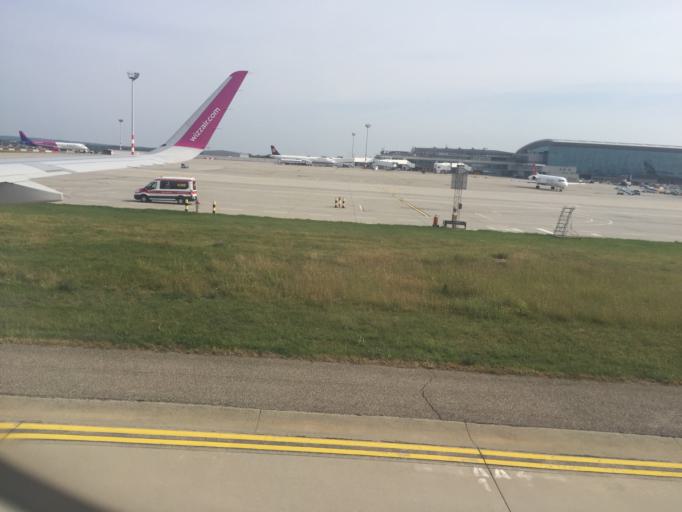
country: HU
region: Pest
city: Vecses
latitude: 47.4368
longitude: 19.2583
